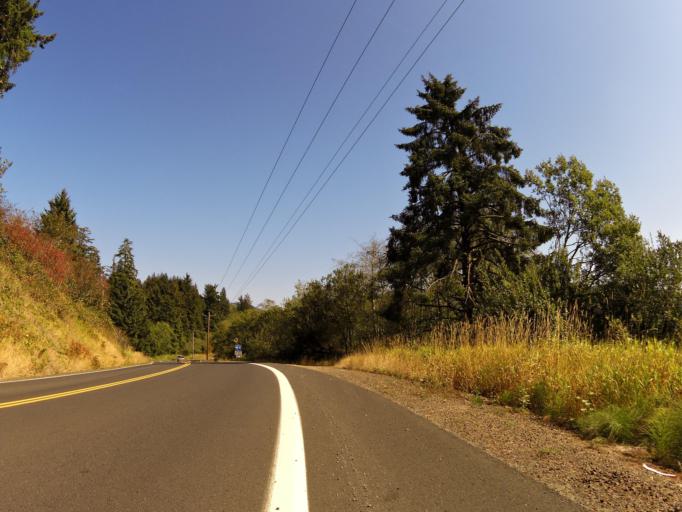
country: US
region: Oregon
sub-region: Tillamook County
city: Pacific City
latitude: 45.1796
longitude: -123.9323
